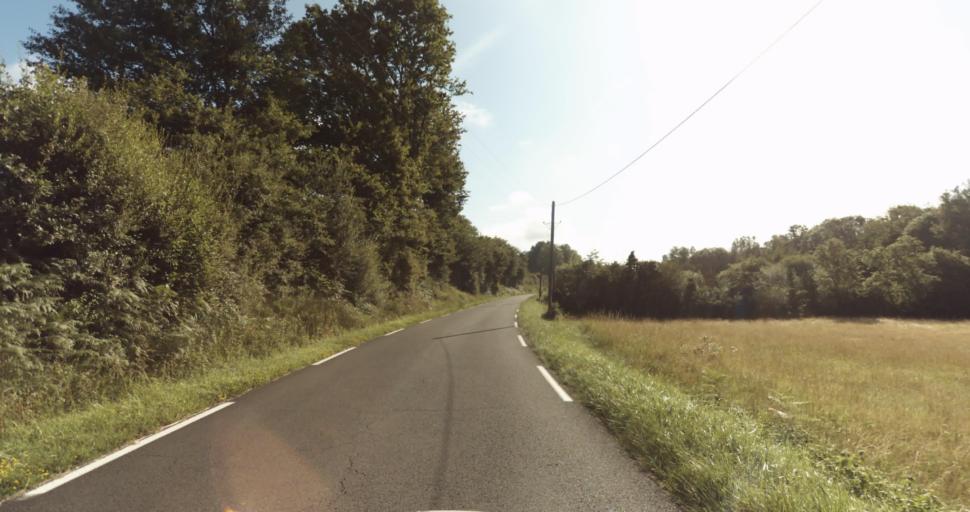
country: FR
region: Aquitaine
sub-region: Departement de la Gironde
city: Bazas
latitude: 44.4276
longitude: -0.2380
